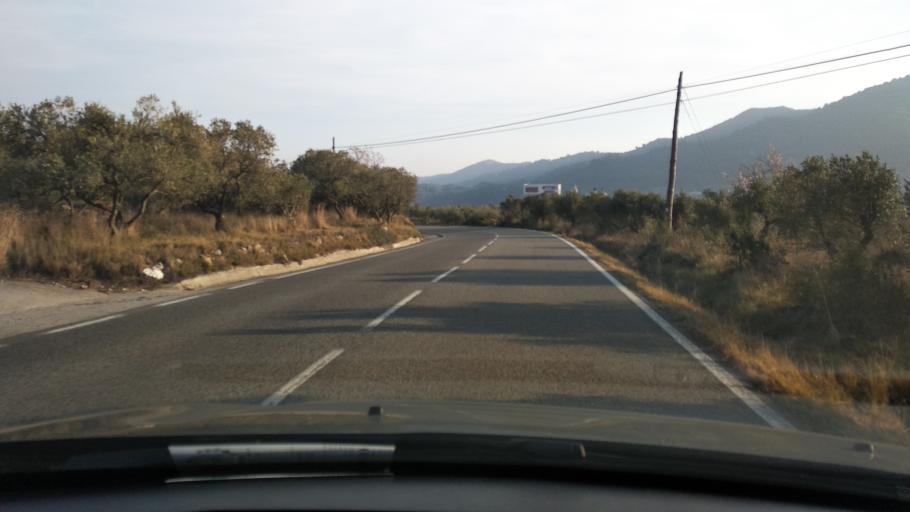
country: ES
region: Catalonia
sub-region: Provincia de Tarragona
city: Alforja
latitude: 41.2165
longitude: 0.9726
